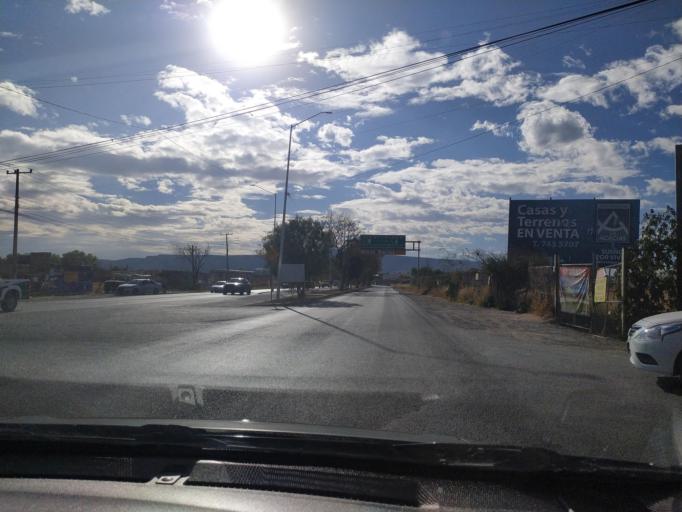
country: LA
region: Oudomxai
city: Muang La
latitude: 21.0322
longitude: 101.8388
